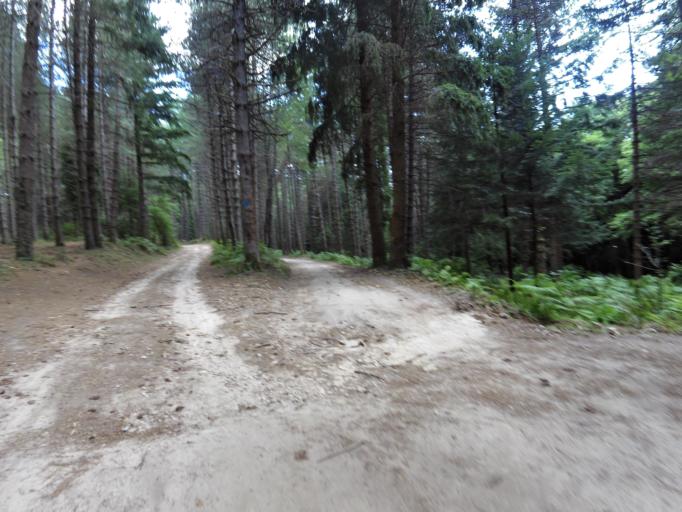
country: IT
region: Calabria
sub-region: Provincia di Vibo-Valentia
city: Nardodipace
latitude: 38.5099
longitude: 16.3791
